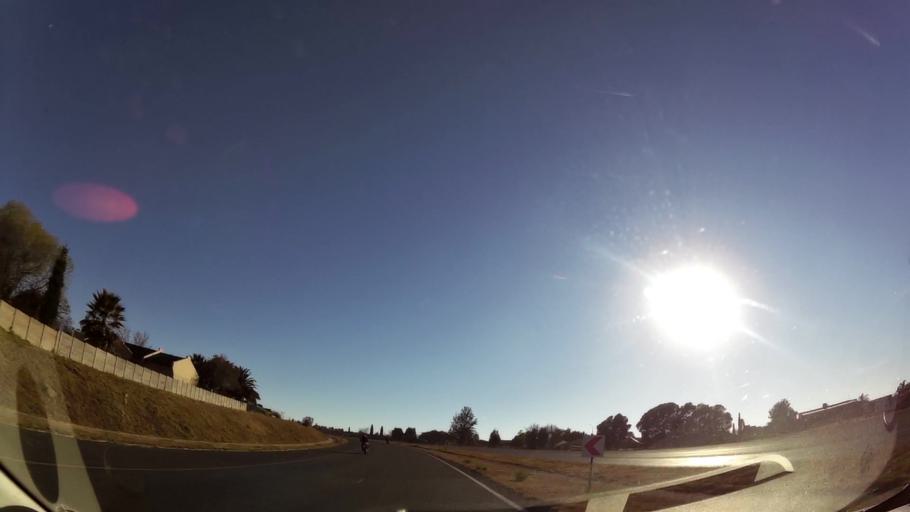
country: ZA
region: Gauteng
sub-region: City of Johannesburg Metropolitan Municipality
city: Modderfontein
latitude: -26.0845
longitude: 28.2047
